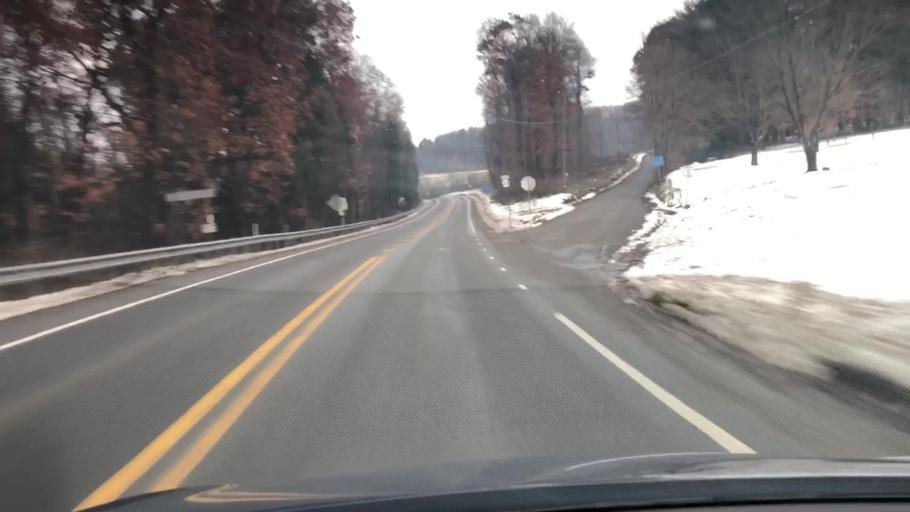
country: US
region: Pennsylvania
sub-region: Jefferson County
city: Brookville
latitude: 41.0403
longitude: -79.2570
